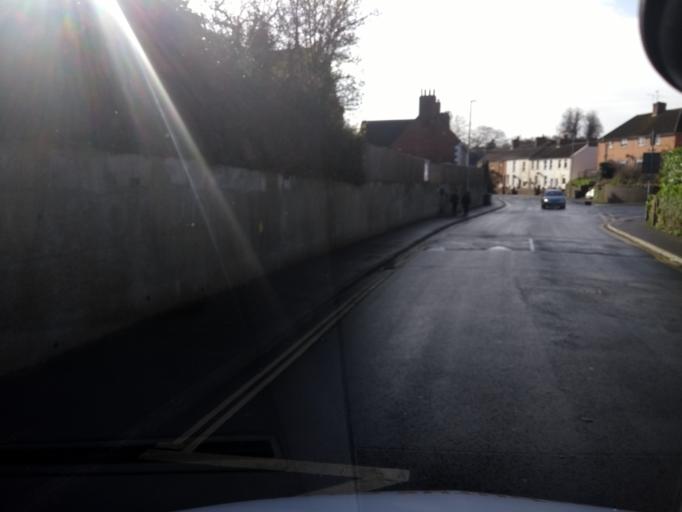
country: GB
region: England
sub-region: Somerset
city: Yeovil
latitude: 50.9464
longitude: -2.6201
